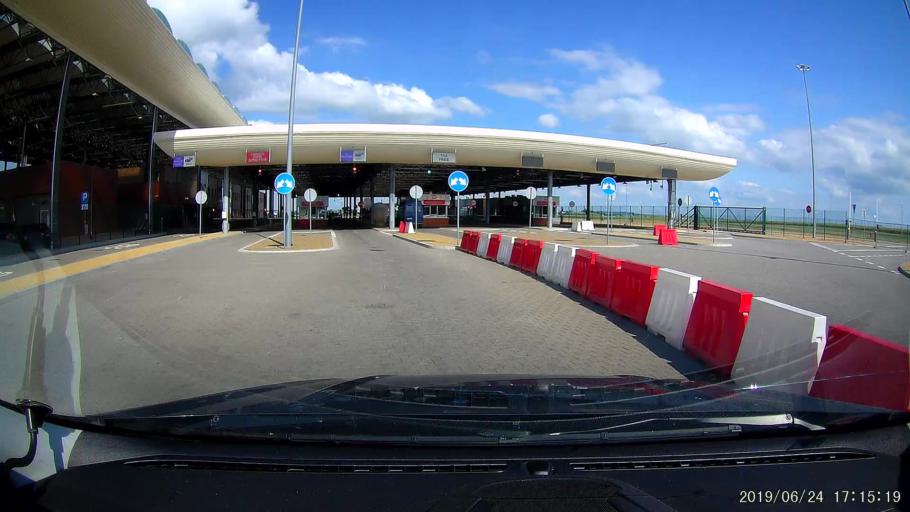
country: PL
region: Lublin Voivodeship
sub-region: Powiat hrubieszowski
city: Dolhobyczow
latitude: 50.5779
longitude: 24.0853
